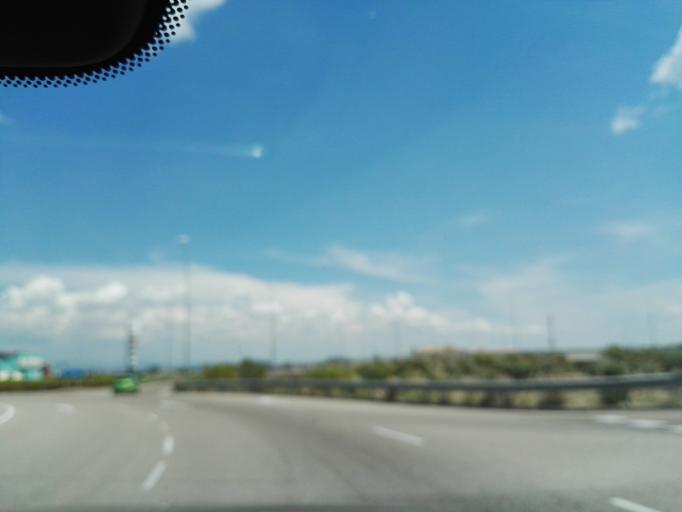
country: ES
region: Aragon
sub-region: Provincia de Zaragoza
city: Montecanal
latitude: 41.6325
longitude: -0.9888
